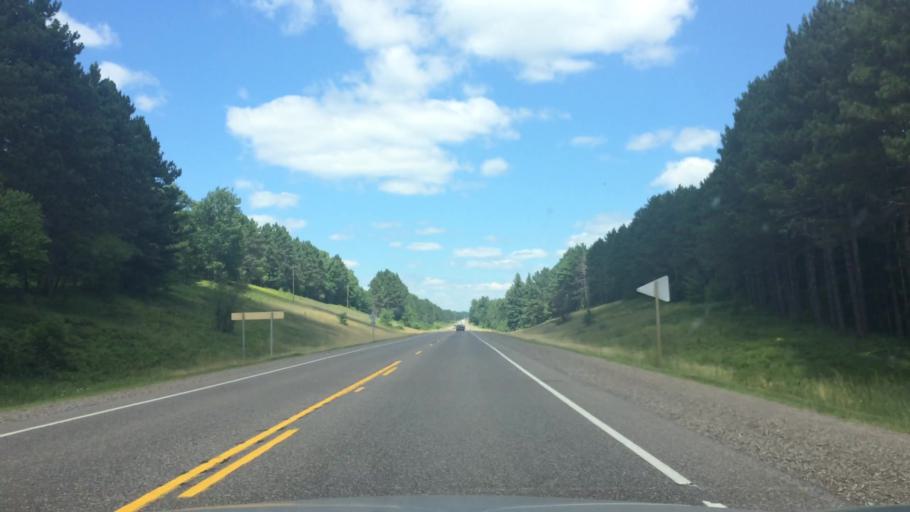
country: US
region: Wisconsin
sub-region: Vilas County
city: Lac du Flambeau
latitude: 45.9535
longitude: -89.7007
